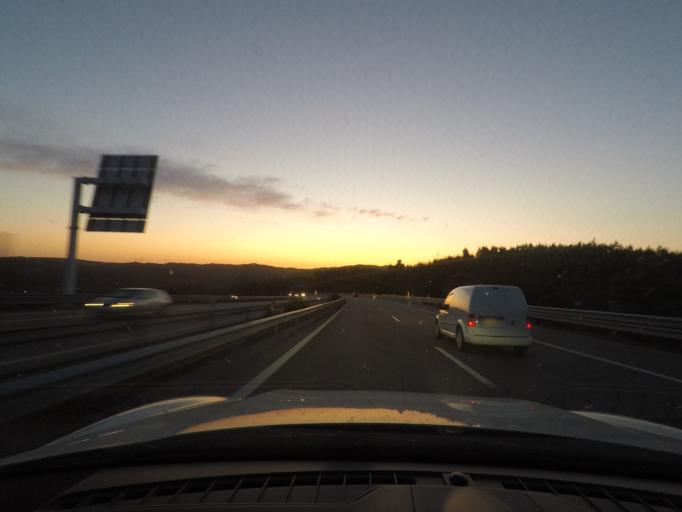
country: PT
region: Porto
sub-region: Valongo
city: Sobrado
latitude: 41.2352
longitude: -8.4457
